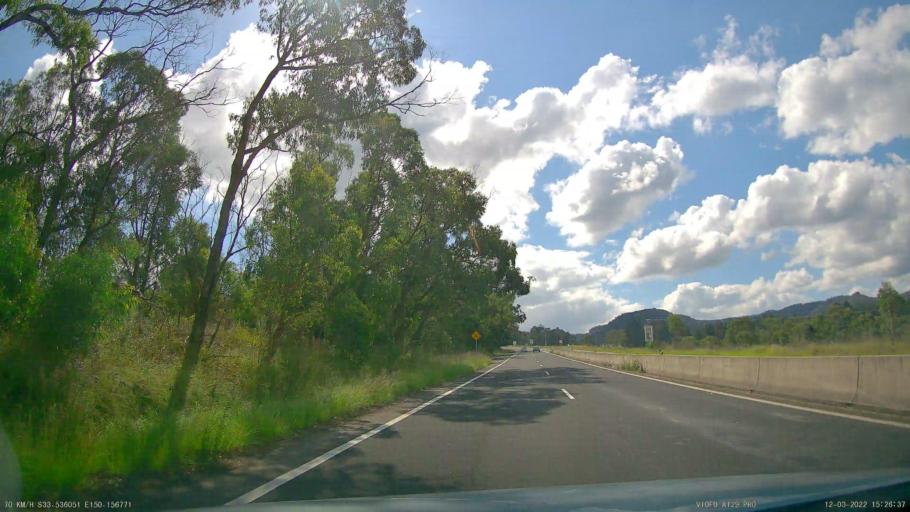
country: AU
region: New South Wales
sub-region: Lithgow
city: Bowenfels
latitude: -33.5358
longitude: 150.1565
